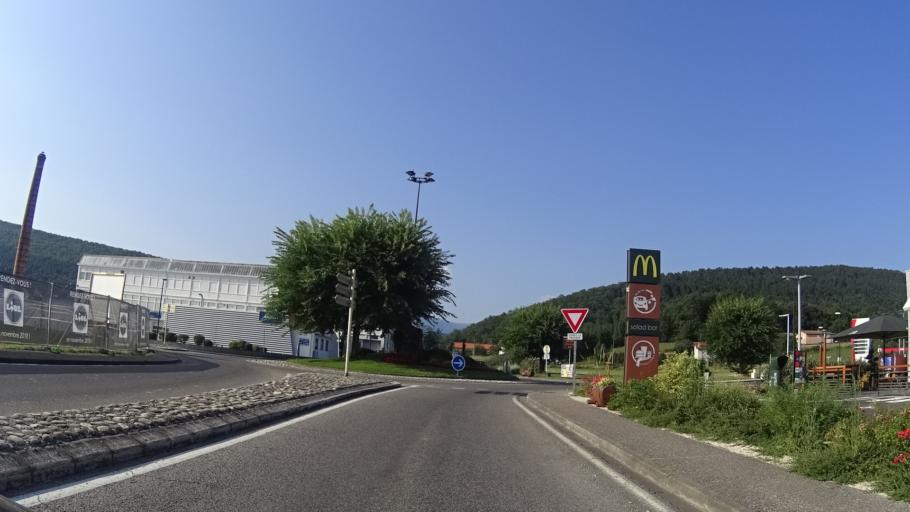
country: FR
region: Midi-Pyrenees
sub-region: Departement de l'Ariege
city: Lavelanet
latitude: 42.9635
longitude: 1.8645
